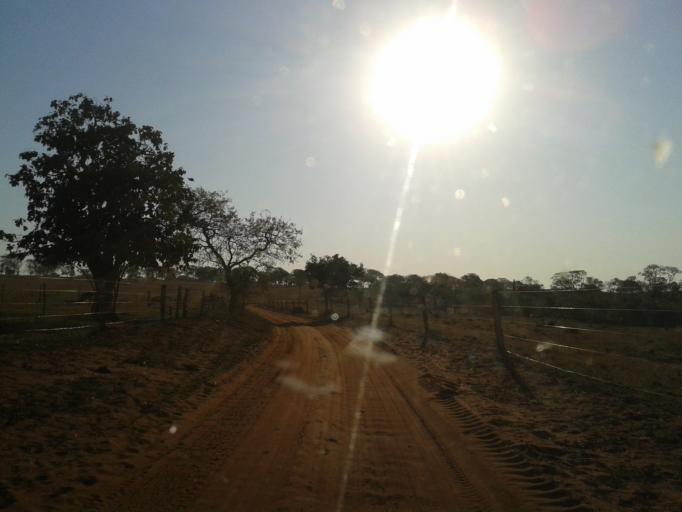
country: BR
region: Minas Gerais
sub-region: Ituiutaba
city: Ituiutaba
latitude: -19.2482
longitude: -49.5807
